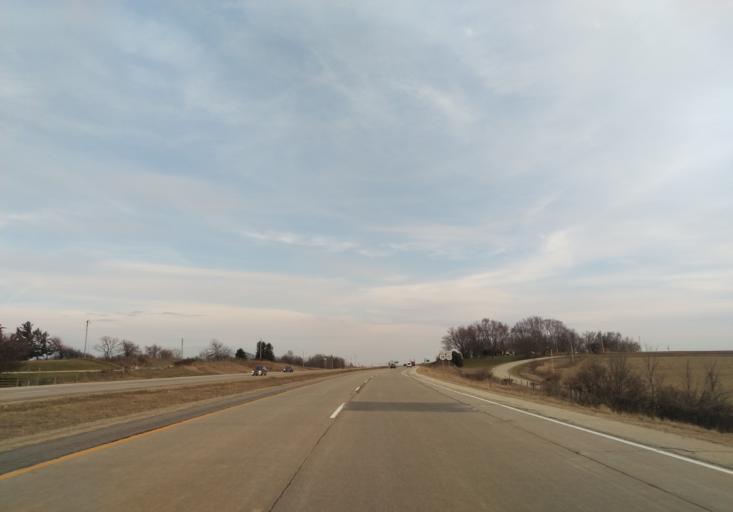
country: US
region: Wisconsin
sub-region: Dane County
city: Mount Horeb
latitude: 42.9961
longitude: -89.6635
